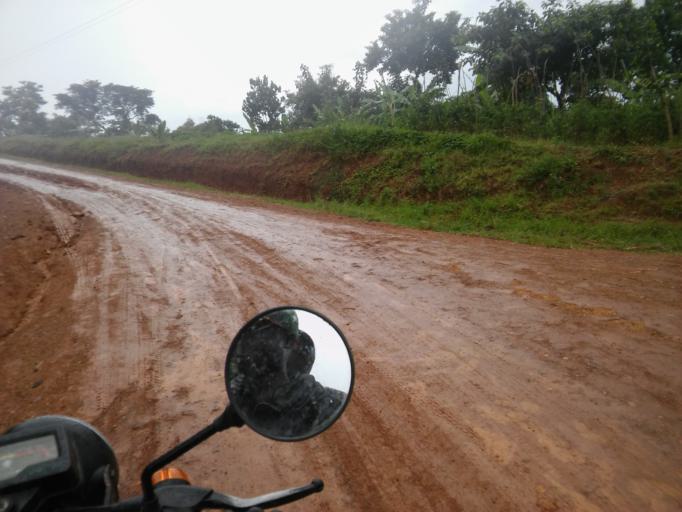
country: UG
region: Eastern Region
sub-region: Bududa District
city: Bududa
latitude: 0.9985
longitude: 34.2501
